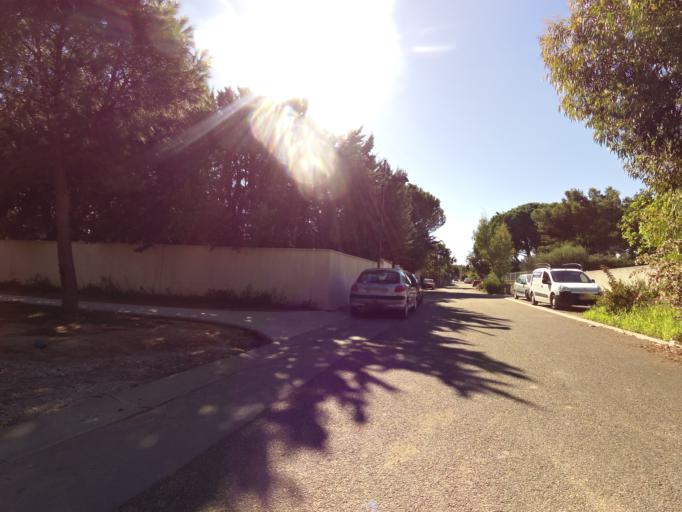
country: FR
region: Languedoc-Roussillon
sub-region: Departement du Gard
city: Gallargues-le-Montueux
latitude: 43.7230
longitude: 4.1801
